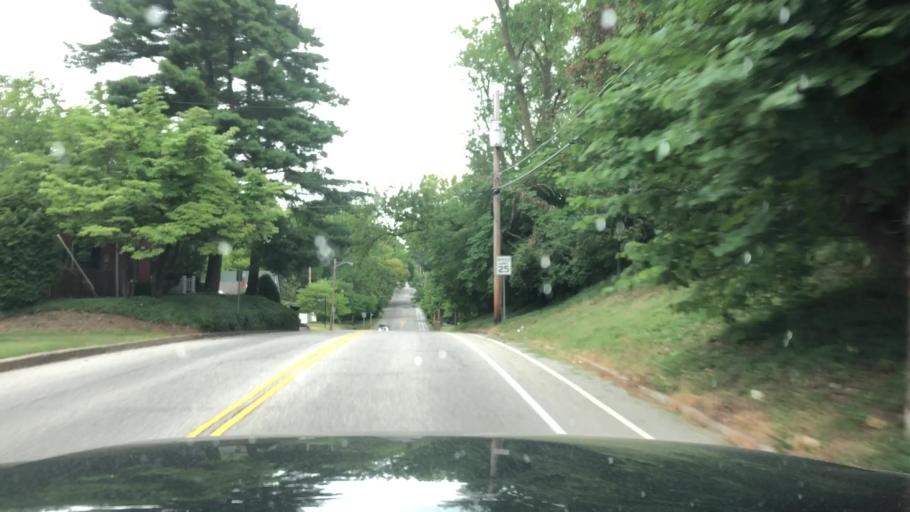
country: US
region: Missouri
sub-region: Saint Charles County
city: Saint Charles
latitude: 38.7908
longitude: -90.4978
